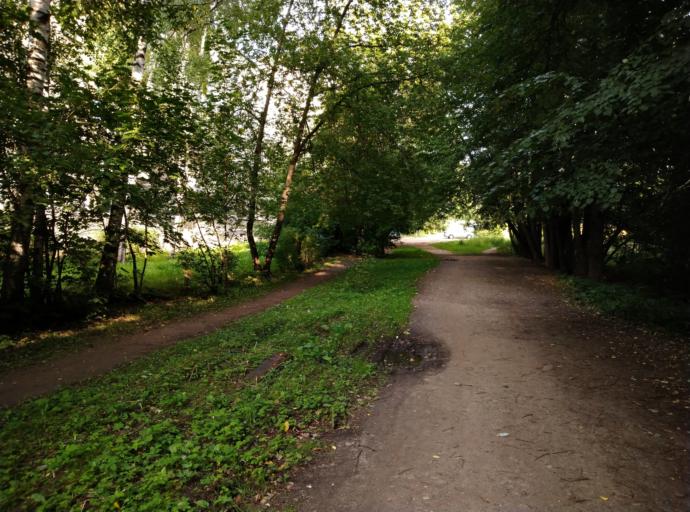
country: RU
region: Kostroma
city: Oktyabr'skiy
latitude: 57.7627
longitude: 40.9669
